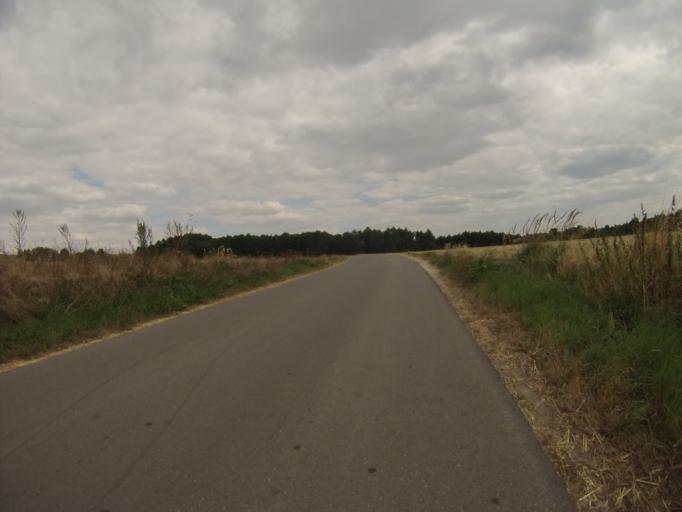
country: PL
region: Swietokrzyskie
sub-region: Powiat staszowski
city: Bogoria
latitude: 50.6868
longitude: 21.2292
